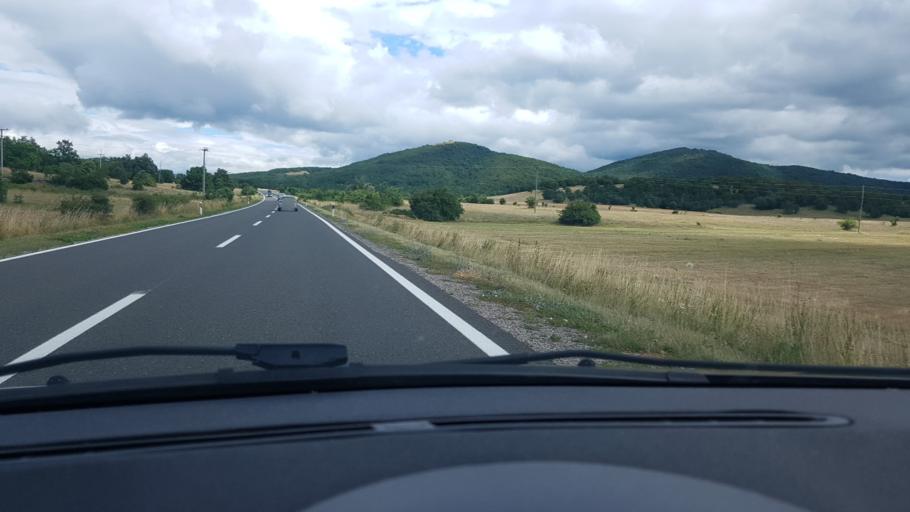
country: HR
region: Zadarska
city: Gracac
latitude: 44.4657
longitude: 15.8013
